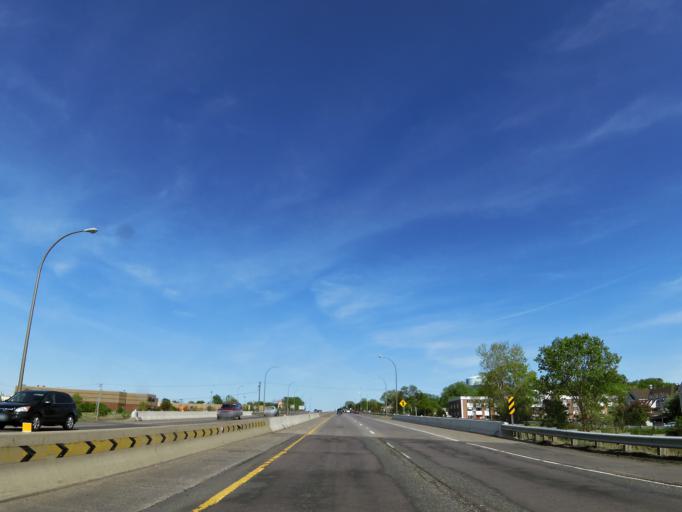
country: US
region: Minnesota
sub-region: Ramsey County
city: North Saint Paul
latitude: 45.0116
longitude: -93.0227
